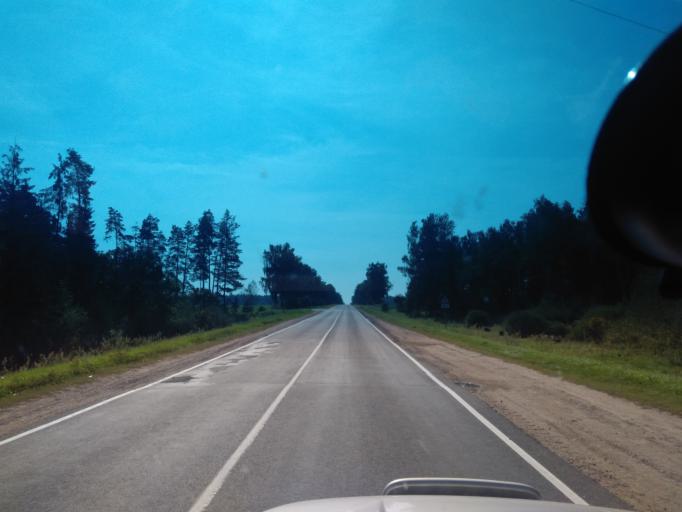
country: BY
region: Minsk
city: Uzda
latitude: 53.3527
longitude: 27.2258
